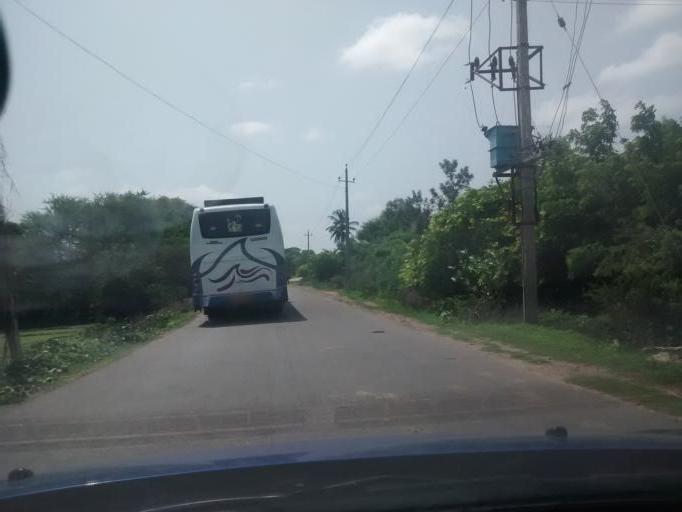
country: IN
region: Karnataka
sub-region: Hassan
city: Konanur
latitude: 12.5817
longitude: 76.1820
